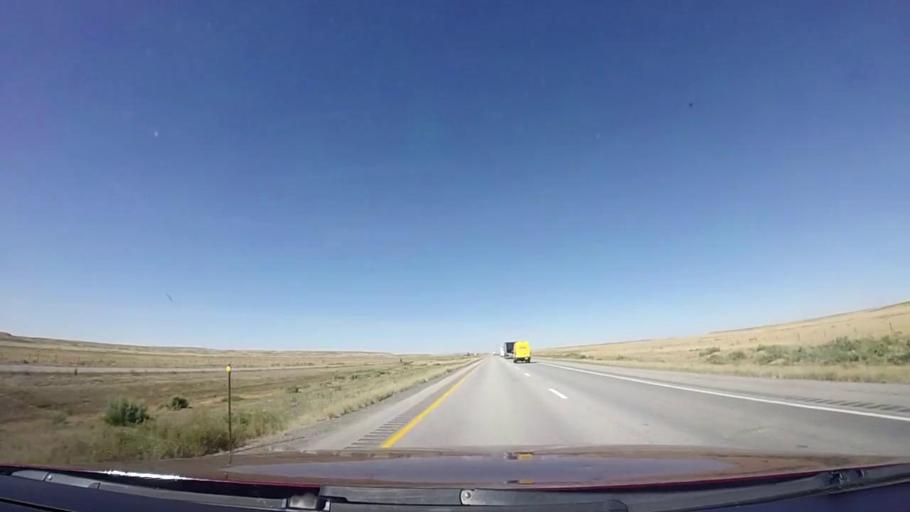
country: US
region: Wyoming
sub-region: Carbon County
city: Rawlins
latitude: 41.6633
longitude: -108.0487
